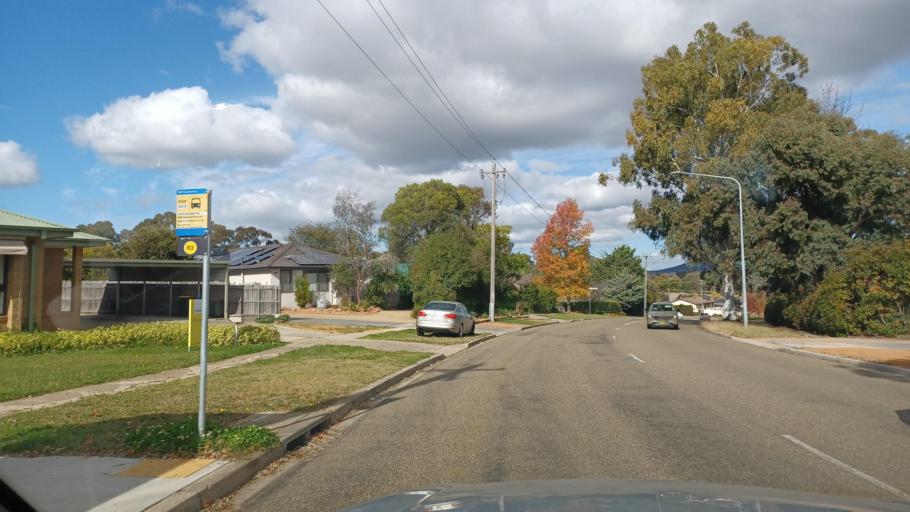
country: AU
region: Australian Capital Territory
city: Belconnen
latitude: -35.2062
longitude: 149.0646
